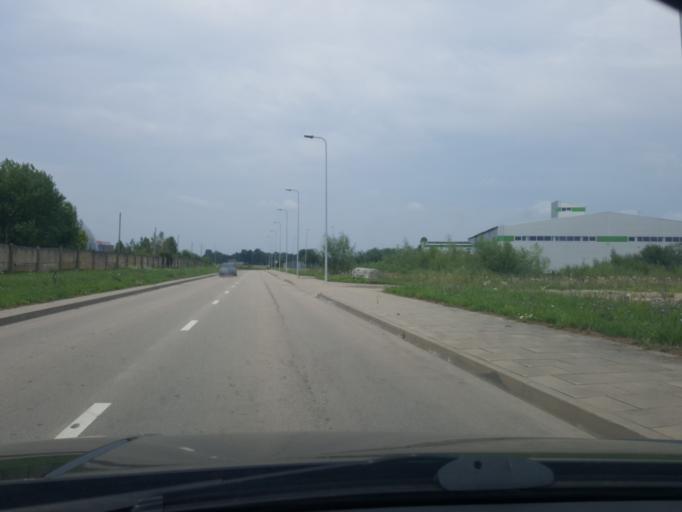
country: LT
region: Alytaus apskritis
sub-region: Alytus
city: Alytus
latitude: 54.4356
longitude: 24.0267
